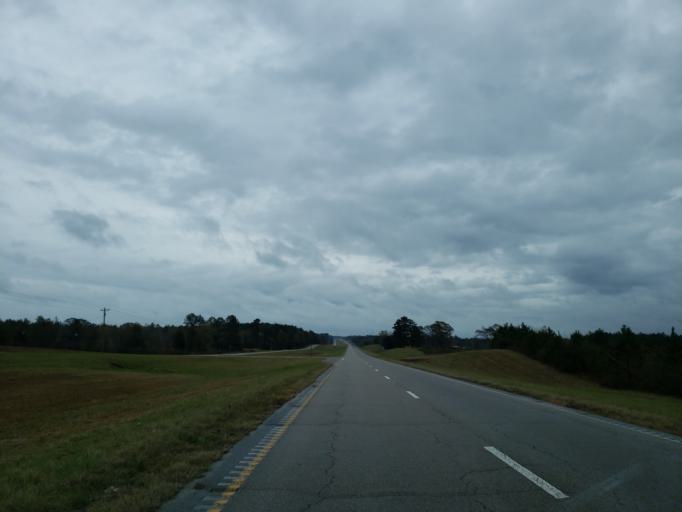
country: US
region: Mississippi
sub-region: Wayne County
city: Waynesboro
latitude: 31.6966
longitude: -88.8618
